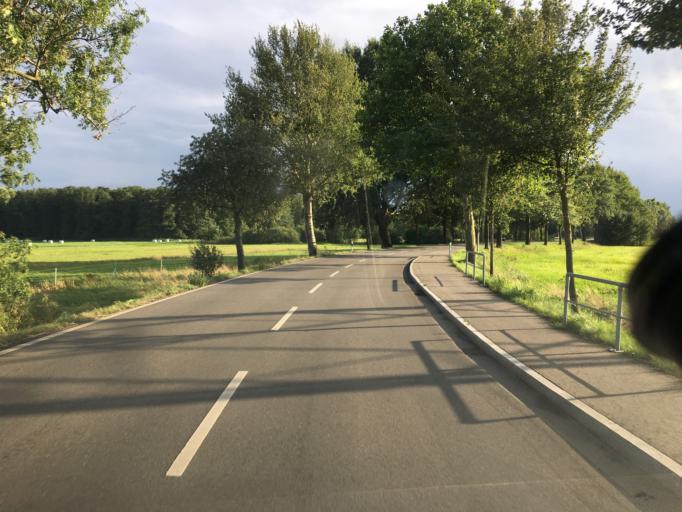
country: DE
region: Lower Saxony
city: Neu Wulmstorf
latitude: 53.4921
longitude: 9.8745
